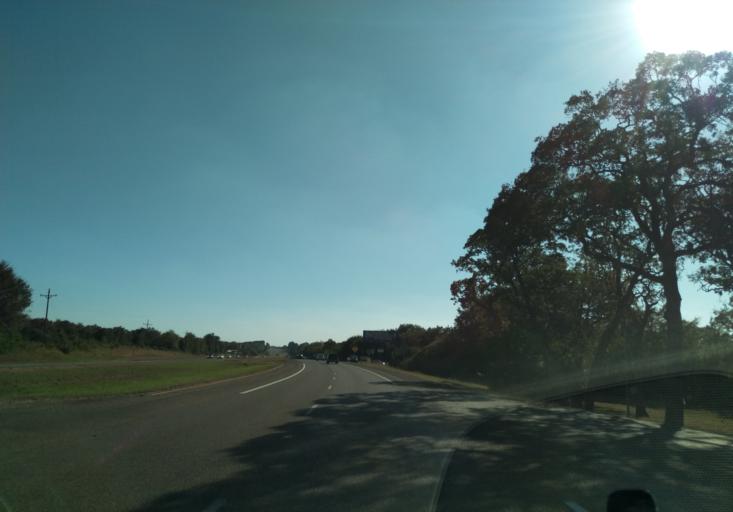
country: US
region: Texas
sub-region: Waller County
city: Hempstead
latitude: 30.2320
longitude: -96.0545
